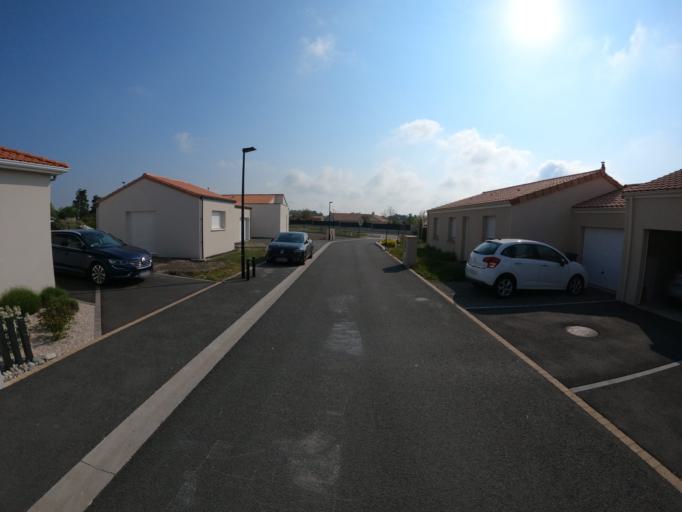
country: FR
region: Pays de la Loire
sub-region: Departement de Maine-et-Loire
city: Torfou
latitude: 47.0317
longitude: -1.1248
